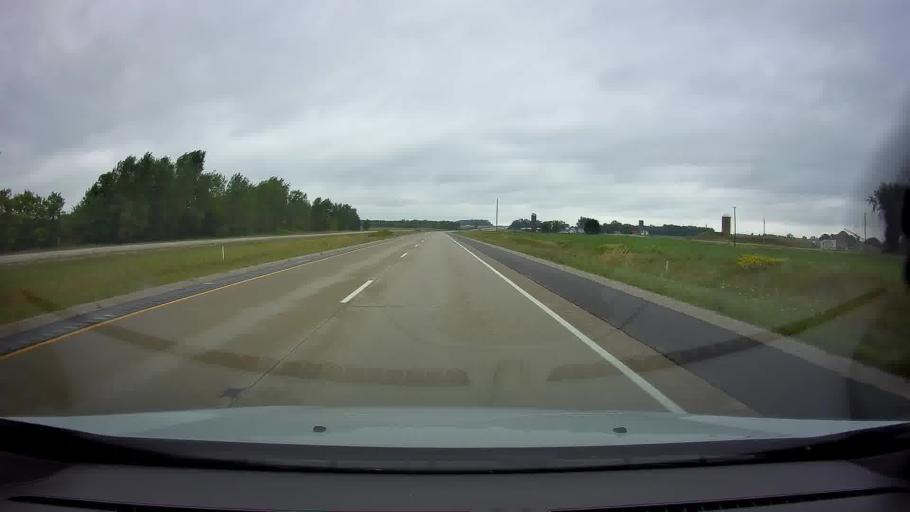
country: US
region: Wisconsin
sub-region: Brown County
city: Pulaski
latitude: 44.6313
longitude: -88.2794
